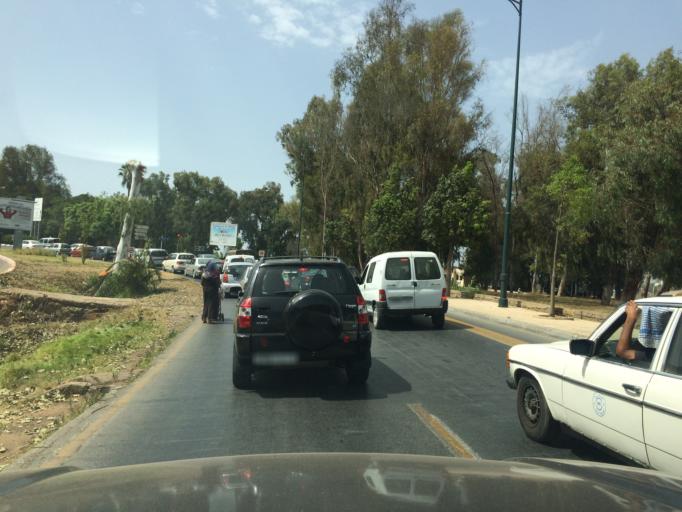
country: MA
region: Rabat-Sale-Zemmour-Zaer
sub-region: Rabat
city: Rabat
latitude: 34.0190
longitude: -6.8183
